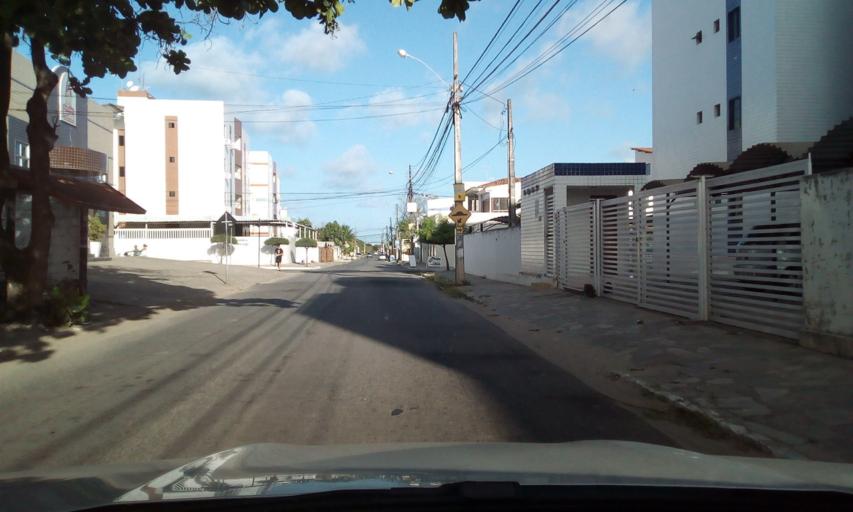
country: BR
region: Paraiba
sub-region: Joao Pessoa
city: Joao Pessoa
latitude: -7.1532
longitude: -34.8324
